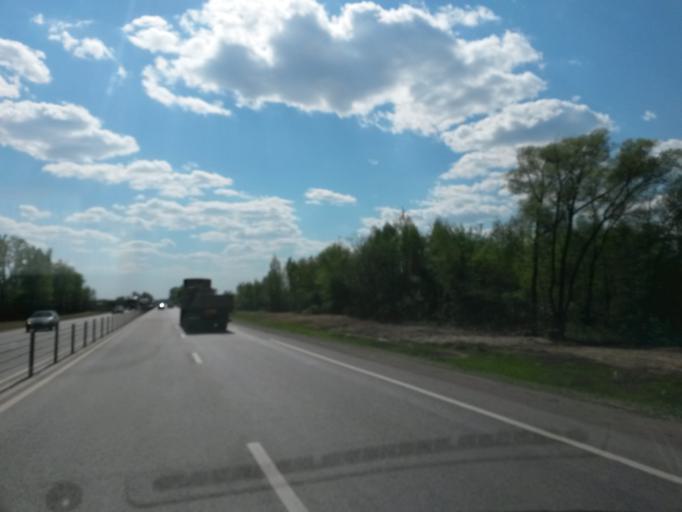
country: RU
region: Jaroslavl
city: Semibratovo
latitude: 57.2803
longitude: 39.5110
